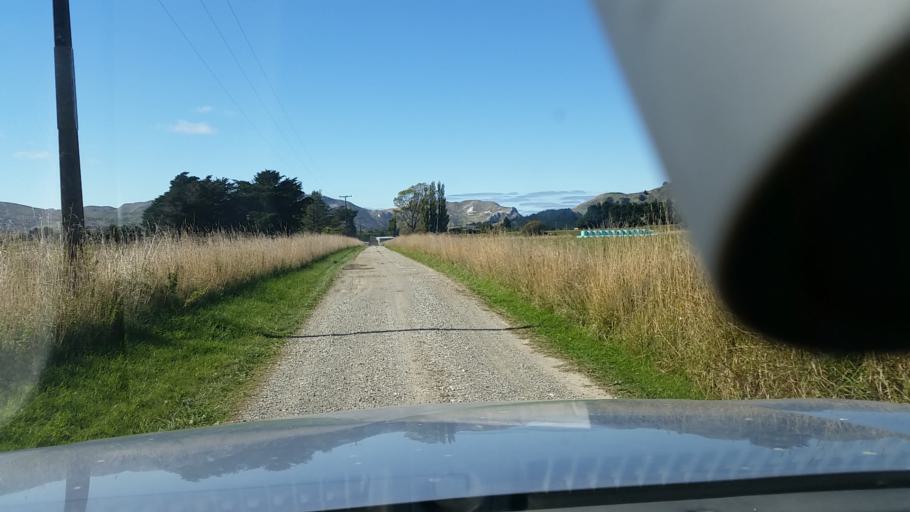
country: NZ
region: Marlborough
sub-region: Marlborough District
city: Blenheim
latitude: -41.8246
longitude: 174.1245
